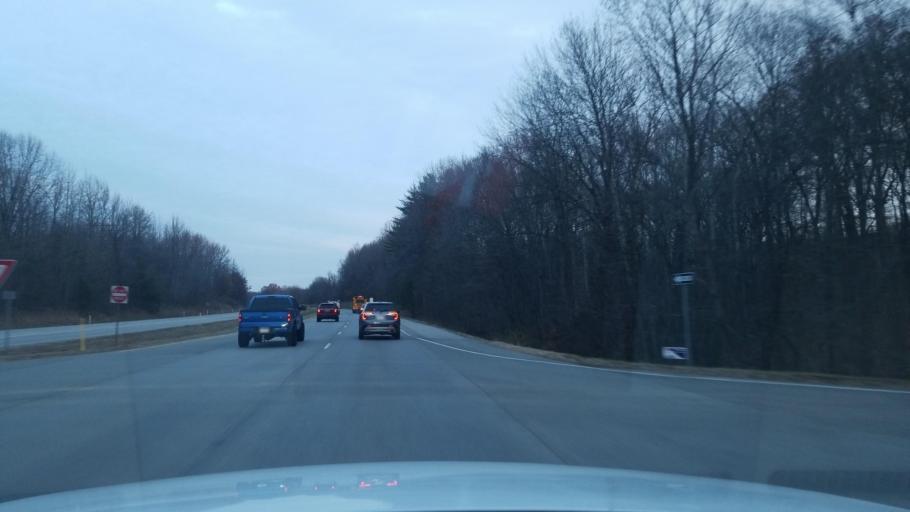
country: US
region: Indiana
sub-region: Vanderburgh County
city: Evansville
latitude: 37.9513
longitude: -87.6994
